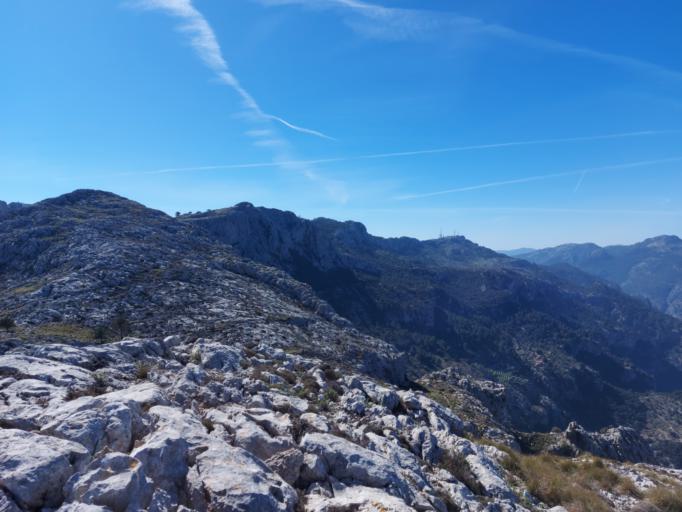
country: ES
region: Balearic Islands
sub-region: Illes Balears
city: Fornalutx
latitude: 39.7597
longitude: 2.7472
